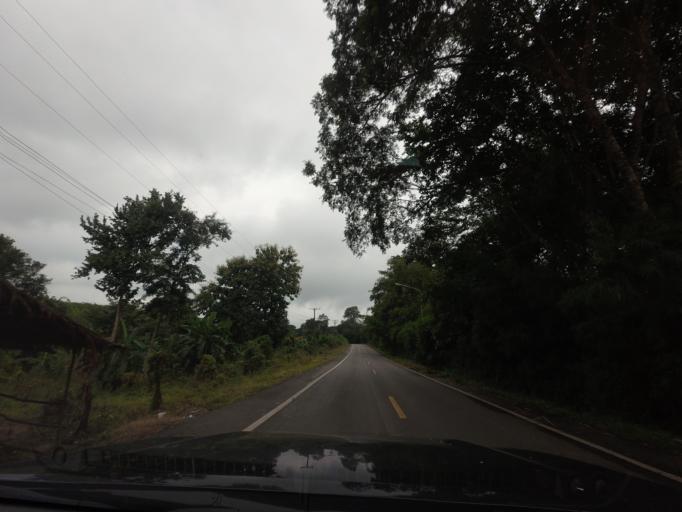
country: TH
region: Nong Khai
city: Sangkhom
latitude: 18.0264
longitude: 102.3580
